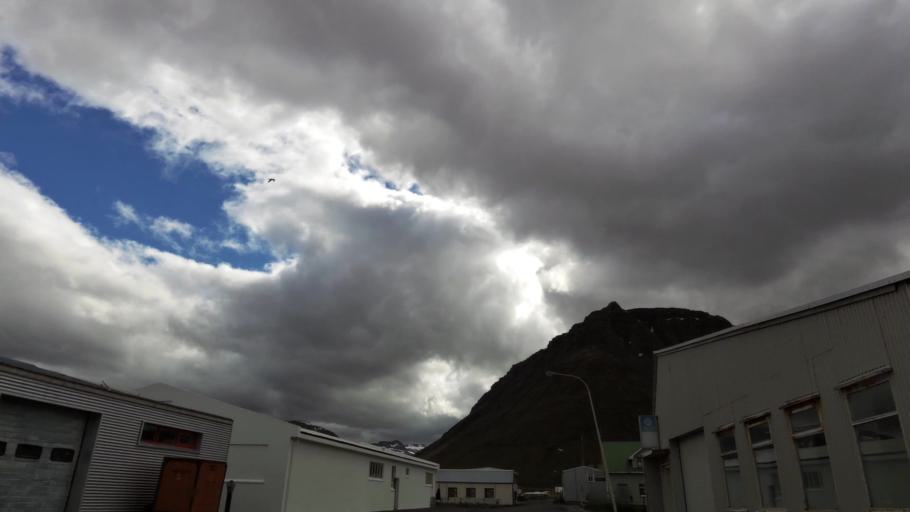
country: IS
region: Westfjords
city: Isafjoerdur
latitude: 66.1582
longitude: -23.2472
